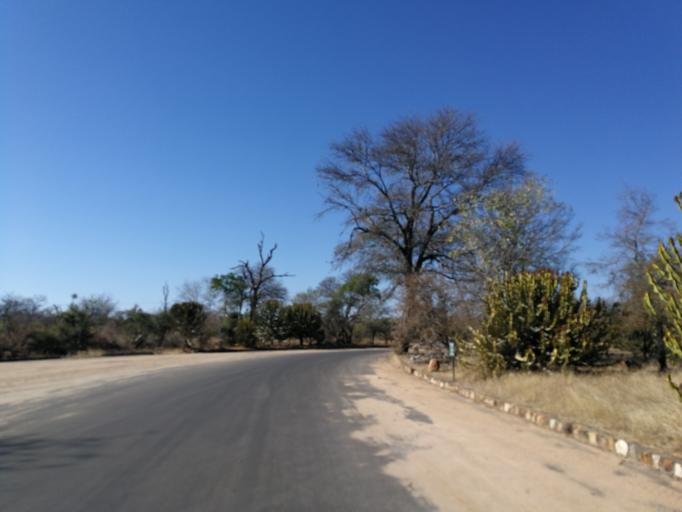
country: ZA
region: Limpopo
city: Thulamahashi
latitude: -24.9811
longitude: 31.4854
